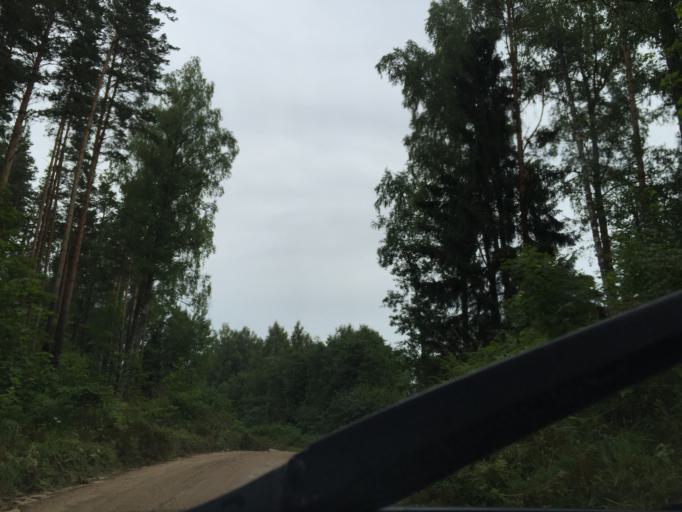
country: LV
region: Dagda
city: Dagda
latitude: 56.2057
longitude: 27.3816
